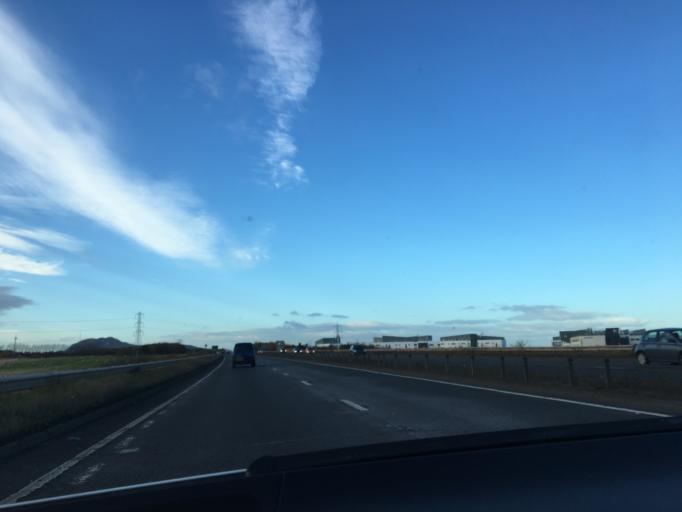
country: GB
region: Scotland
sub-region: East Lothian
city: Musselburgh
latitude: 55.9275
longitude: -3.0695
